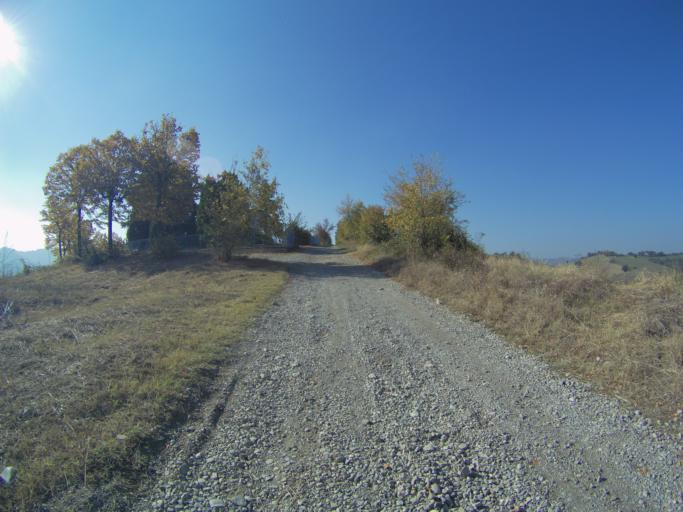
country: IT
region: Emilia-Romagna
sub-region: Provincia di Reggio Emilia
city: Vezzano sul Crostolo
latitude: 44.6157
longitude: 10.5487
